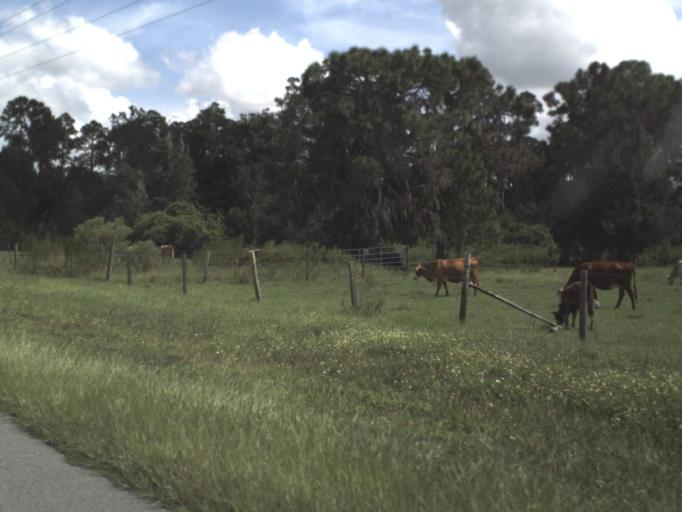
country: US
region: Florida
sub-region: Hardee County
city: Wauchula
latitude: 27.4704
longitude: -82.0618
